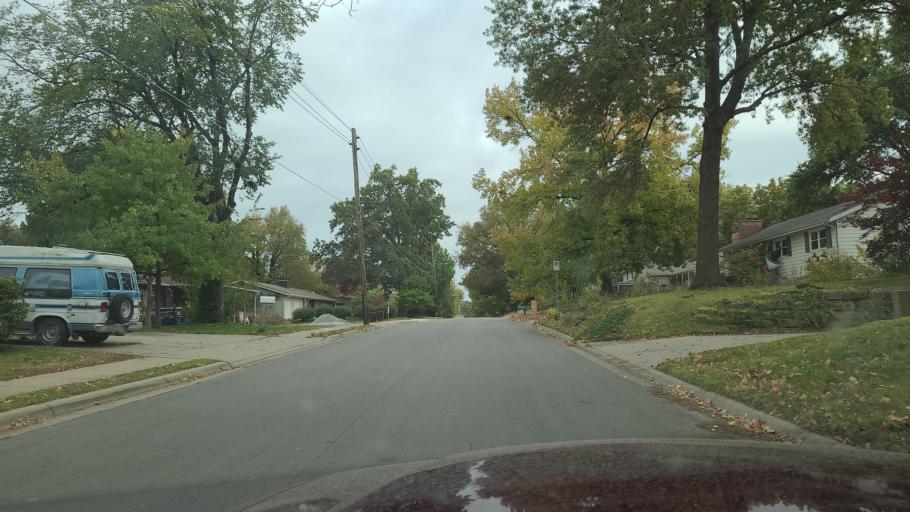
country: US
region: Kansas
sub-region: Douglas County
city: Lawrence
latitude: 38.9381
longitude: -95.2465
